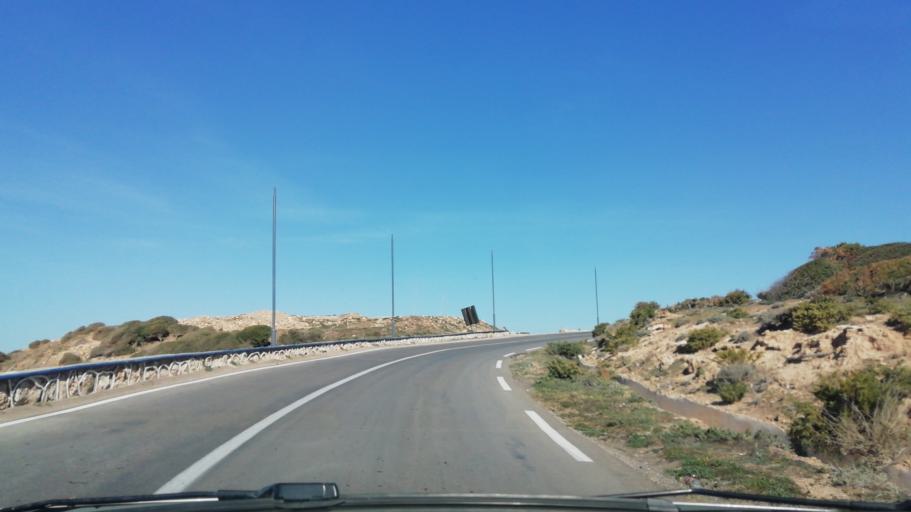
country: DZ
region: Ain Temouchent
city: El Amria
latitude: 35.6419
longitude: -1.0579
